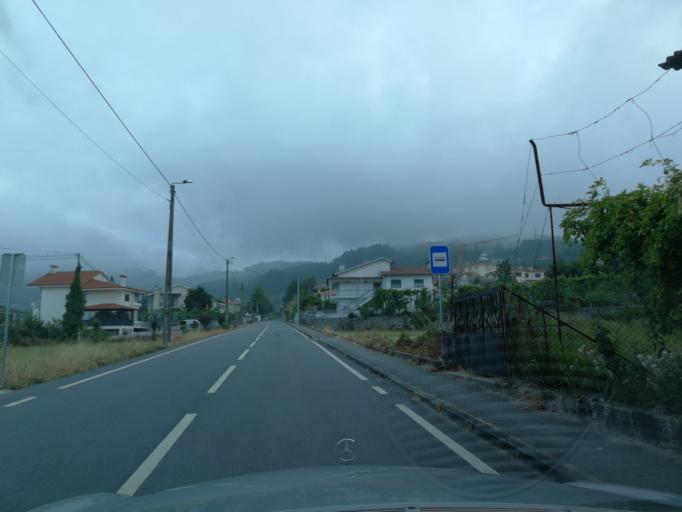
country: PT
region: Braga
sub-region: Guimaraes
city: Ponte
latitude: 41.5134
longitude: -8.3556
